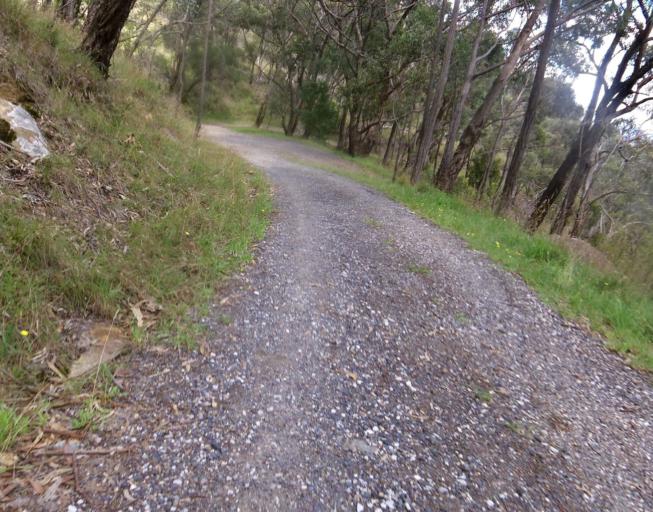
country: AU
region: Victoria
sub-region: Yarra Ranges
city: Montrose
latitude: -37.8220
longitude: 145.3479
